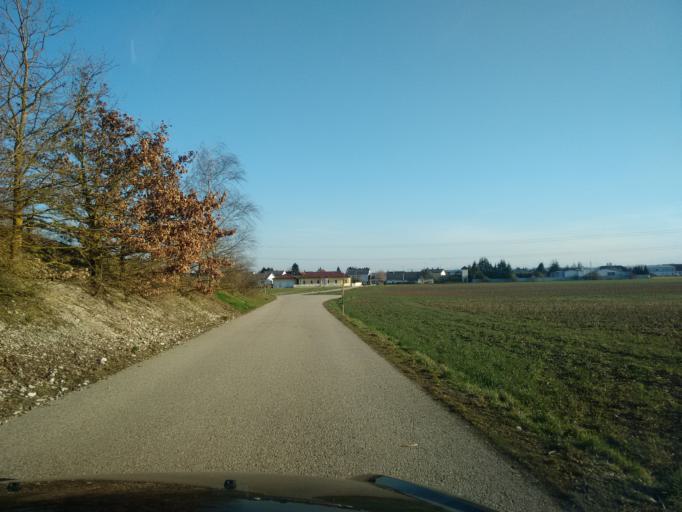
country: AT
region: Upper Austria
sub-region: Wels-Land
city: Marchtrenk
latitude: 48.2059
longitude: 14.1409
